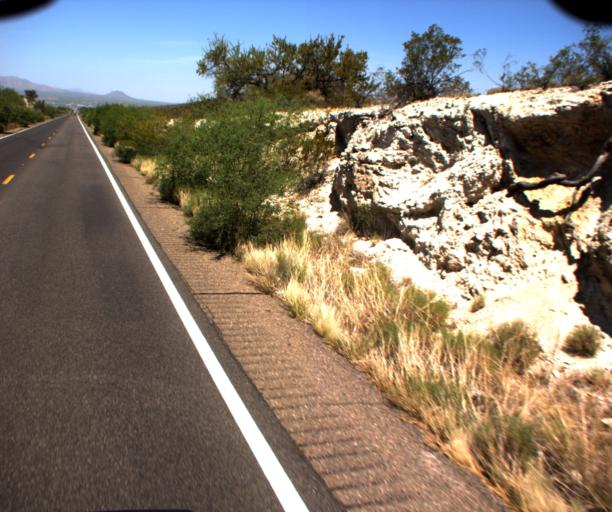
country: US
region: Arizona
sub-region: Gila County
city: Peridot
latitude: 33.2874
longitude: -110.3868
